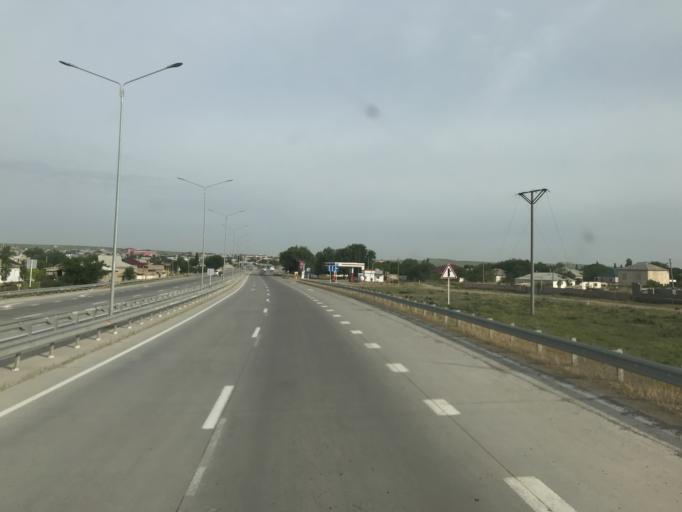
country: KZ
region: Ongtustik Qazaqstan
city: Qazyqurt
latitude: 41.7831
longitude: 69.4005
